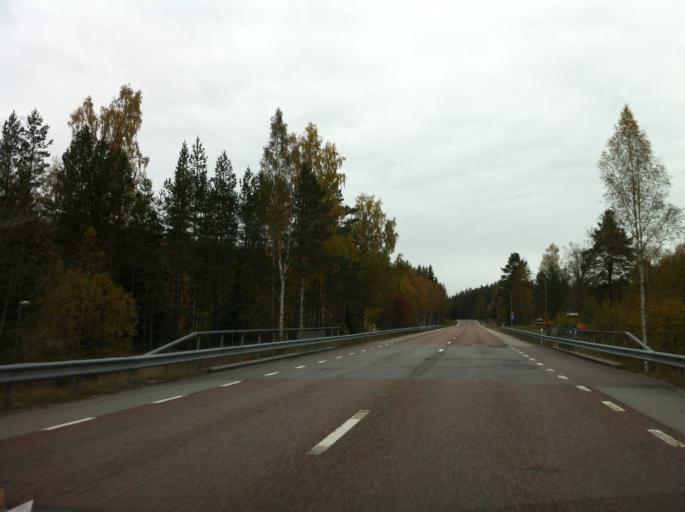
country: SE
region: Dalarna
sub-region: Ludvika Kommun
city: Grangesberg
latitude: 59.9873
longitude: 15.0200
